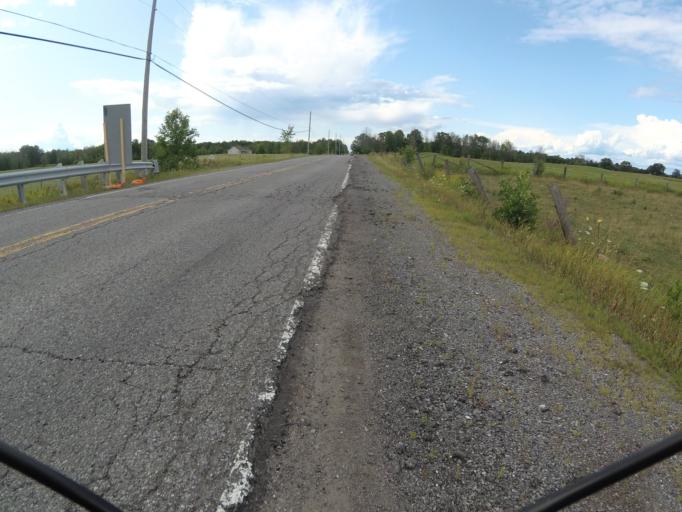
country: CA
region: Ontario
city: Arnprior
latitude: 45.4803
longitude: -76.0996
